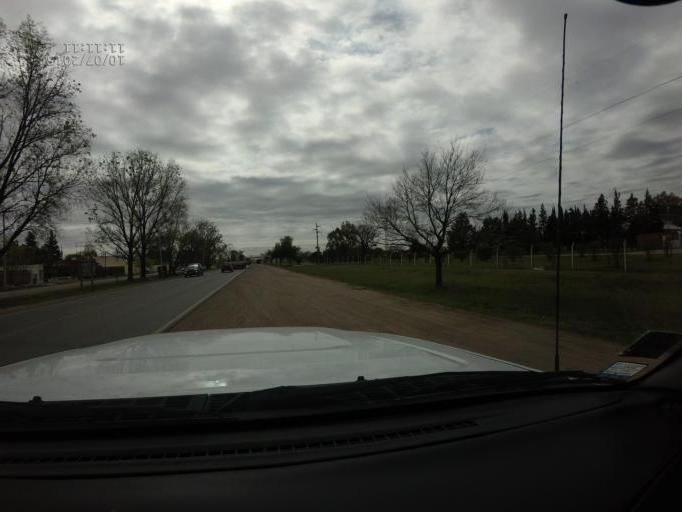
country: AR
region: Cordoba
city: Jesus Maria
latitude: -30.9892
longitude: -64.0941
